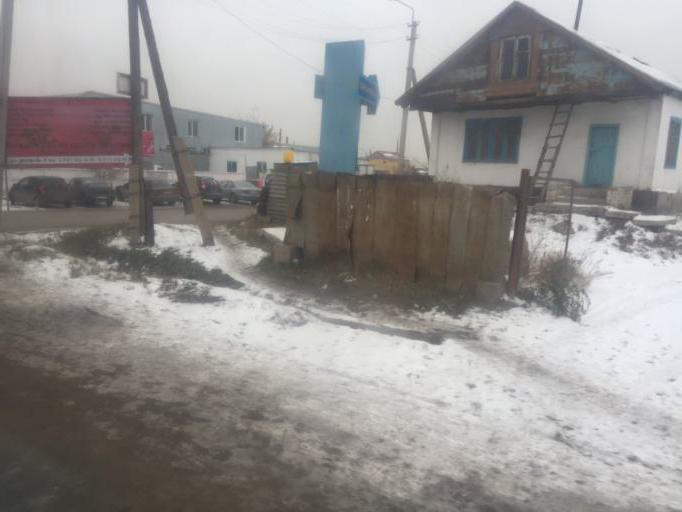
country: KZ
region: Astana Qalasy
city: Astana
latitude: 51.2029
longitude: 71.4118
